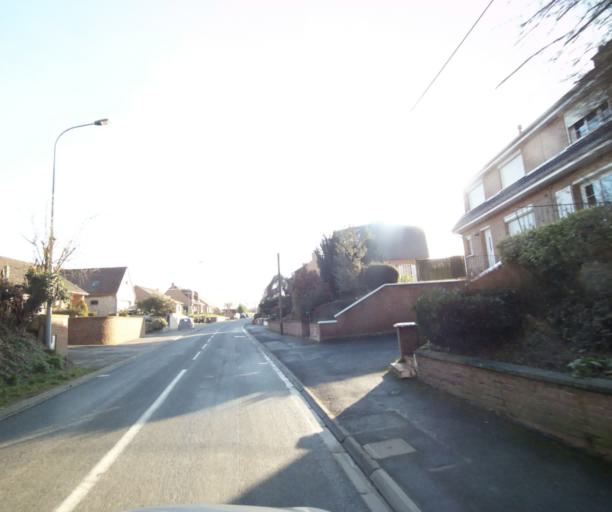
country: FR
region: Nord-Pas-de-Calais
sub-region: Departement du Nord
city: Saultain
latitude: 50.3343
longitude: 3.5746
